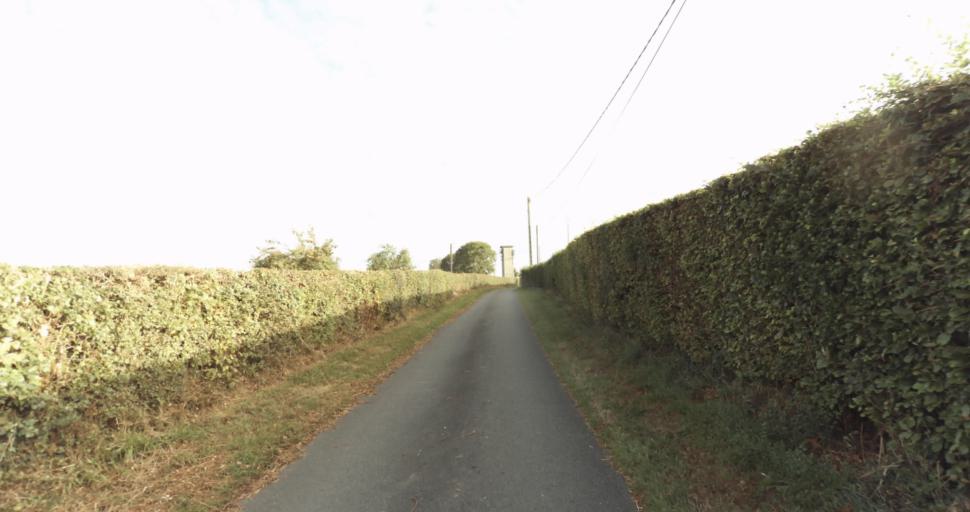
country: FR
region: Lower Normandy
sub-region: Departement de l'Orne
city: Vimoutiers
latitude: 48.8815
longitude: 0.2356
